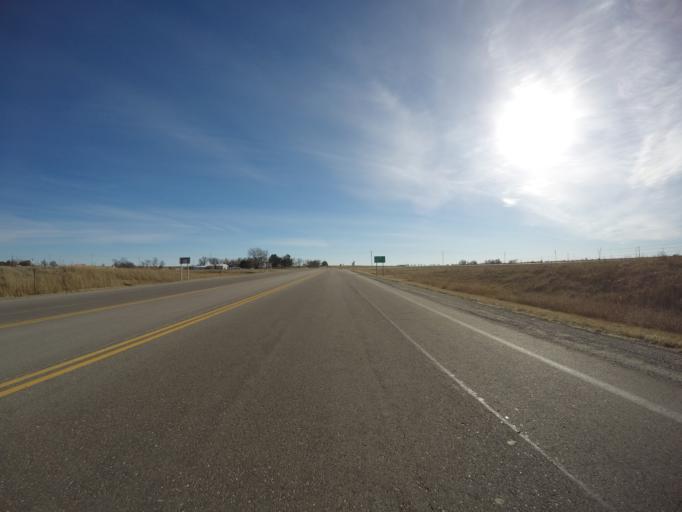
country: US
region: Kansas
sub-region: Marion County
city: Hillsboro
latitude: 38.3646
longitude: -97.2246
